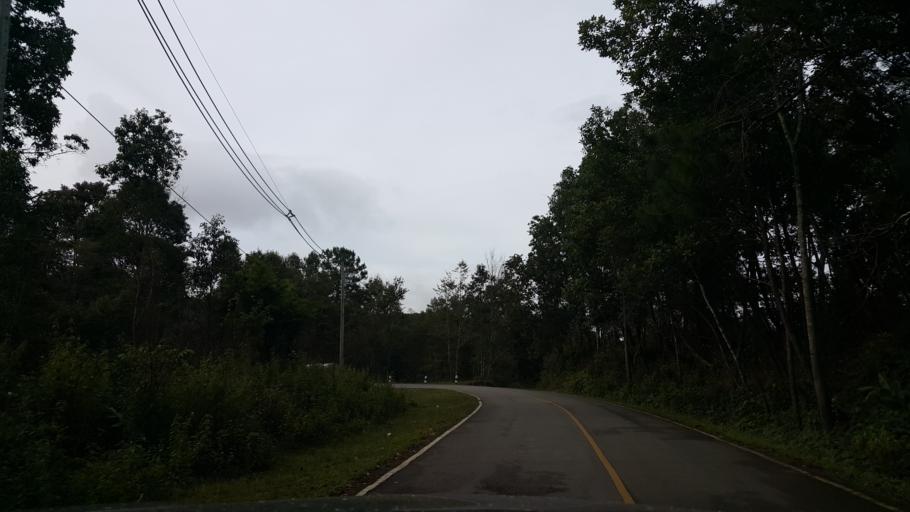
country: TH
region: Chiang Mai
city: Chaem Luang
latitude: 18.9181
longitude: 98.4804
